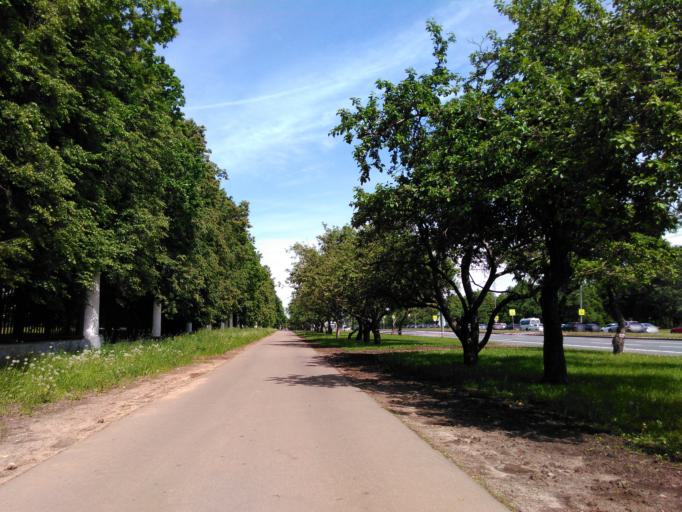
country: RU
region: Moskovskaya
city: Semenovskoye
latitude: 55.6964
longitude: 37.5397
